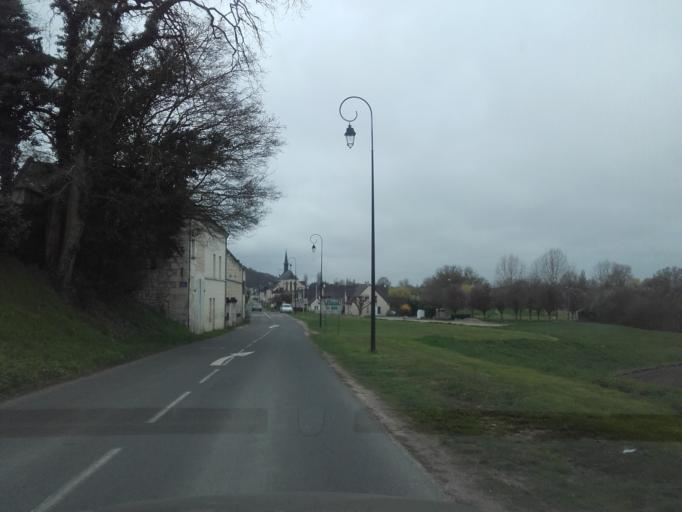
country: FR
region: Centre
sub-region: Departement d'Indre-et-Loire
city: Huismes
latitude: 47.2539
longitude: 0.3045
